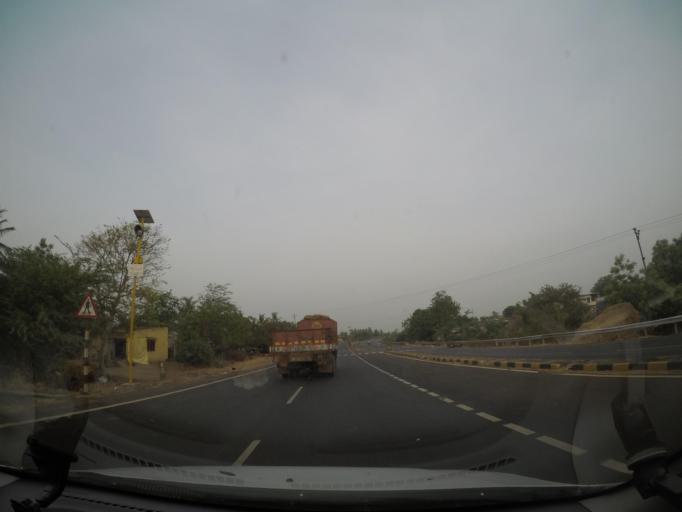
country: IN
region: Andhra Pradesh
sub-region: Krishna
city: Gannavaram
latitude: 16.6095
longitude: 80.9203
